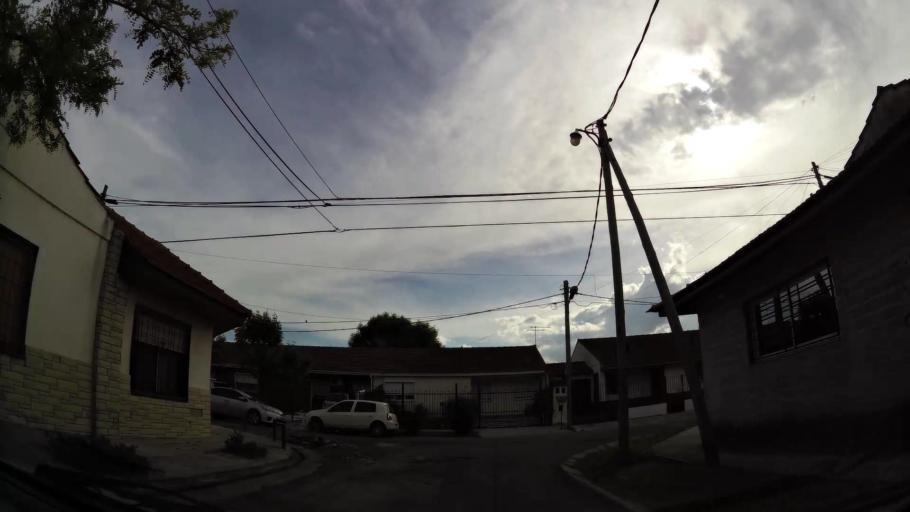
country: AR
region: Buenos Aires
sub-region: Partido de Quilmes
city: Quilmes
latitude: -34.7522
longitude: -58.2765
